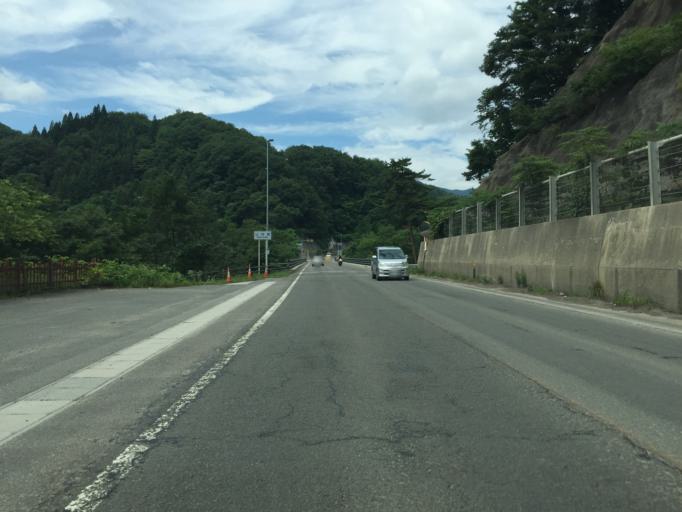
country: JP
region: Fukushima
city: Fukushima-shi
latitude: 37.8396
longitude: 140.3707
